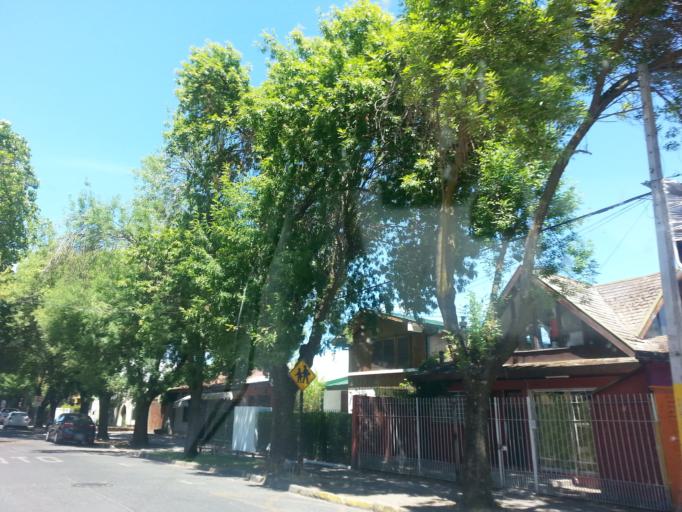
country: CL
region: Biobio
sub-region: Provincia de Nuble
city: Chillan
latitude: -36.6058
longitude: -72.0988
